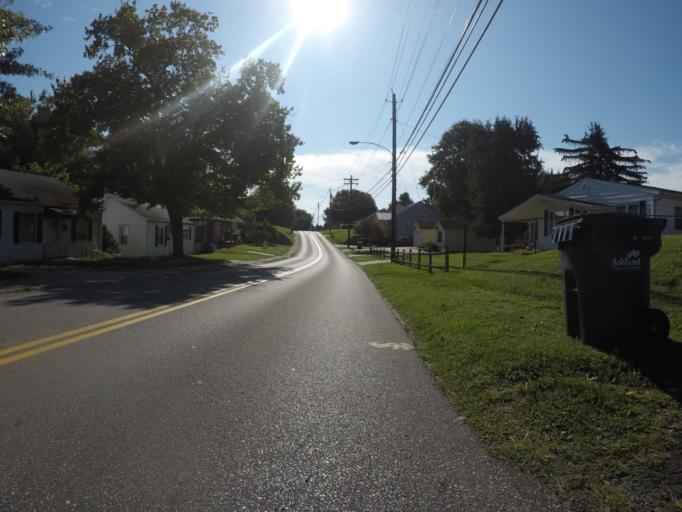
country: US
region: Kentucky
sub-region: Boyd County
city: Ashland
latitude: 38.4514
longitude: -82.6324
